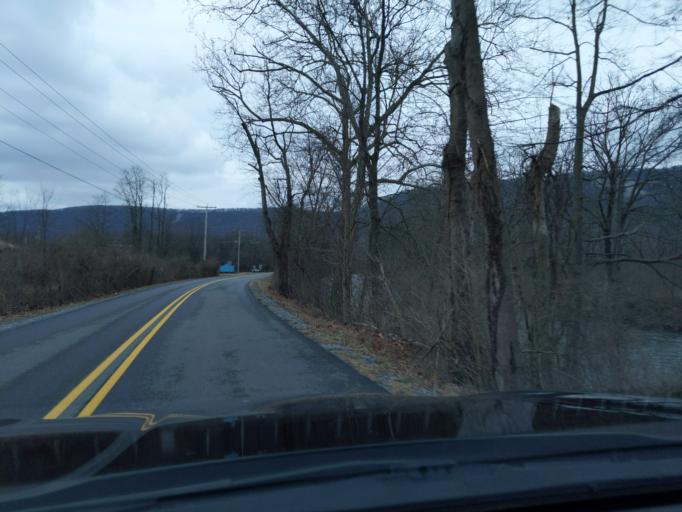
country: US
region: Pennsylvania
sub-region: Blair County
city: Tipton
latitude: 40.6281
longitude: -78.3046
